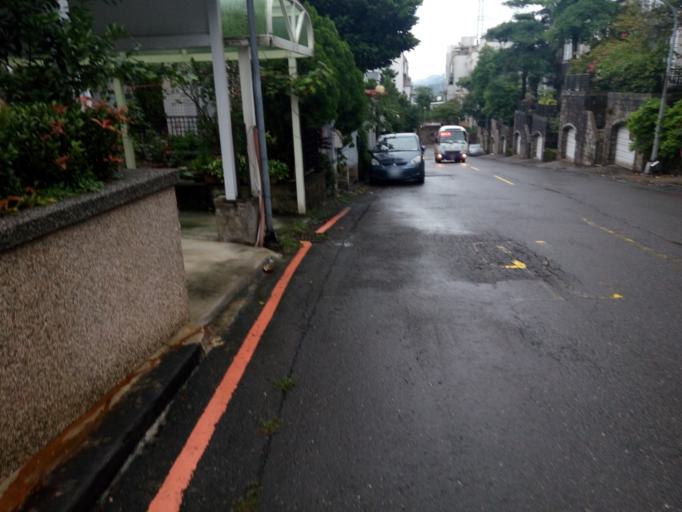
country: TW
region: Taiwan
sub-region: Keelung
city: Keelung
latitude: 25.0581
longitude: 121.6680
